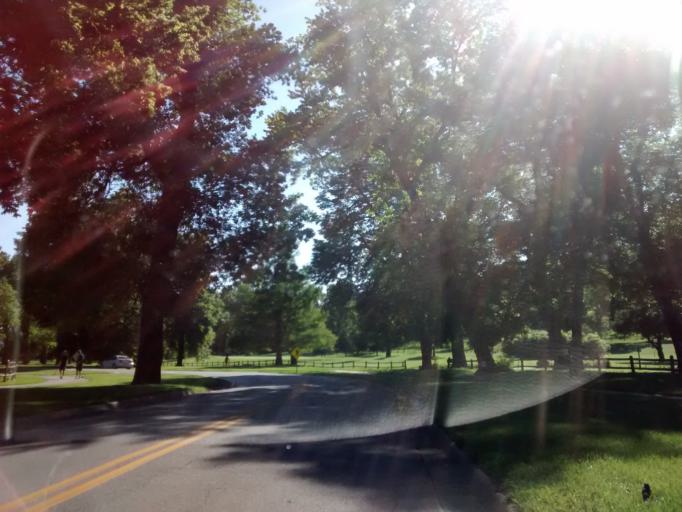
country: US
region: Nebraska
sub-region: Douglas County
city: Ralston
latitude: 41.2516
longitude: -96.0133
